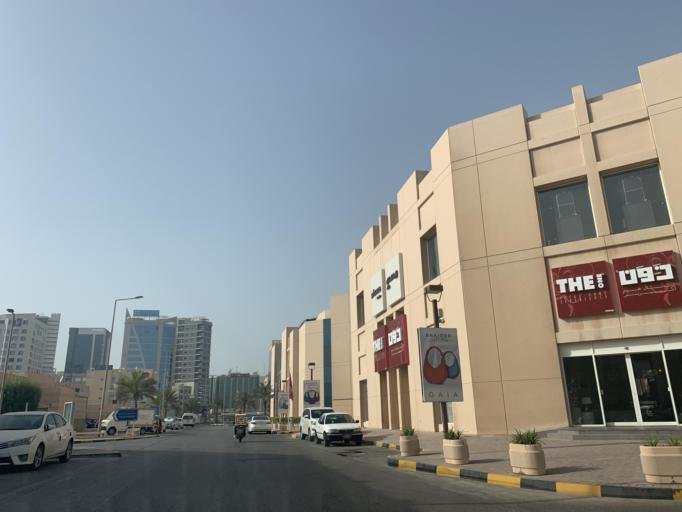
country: BH
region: Manama
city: Jidd Hafs
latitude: 26.2332
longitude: 50.5393
